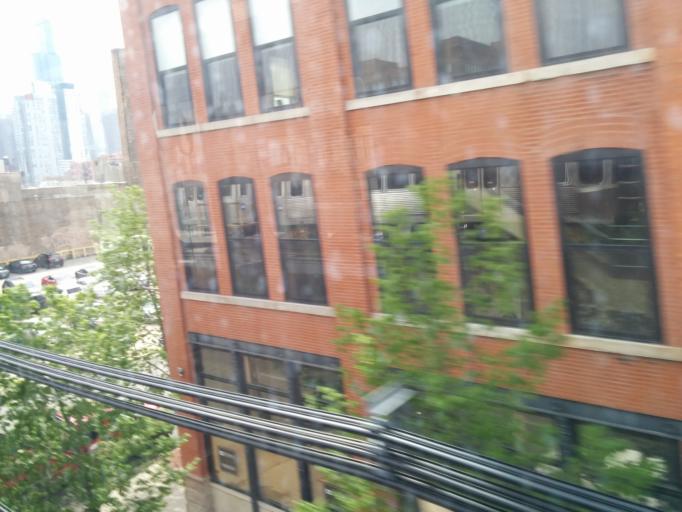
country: US
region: Illinois
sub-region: Cook County
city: Chicago
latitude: 41.8854
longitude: -87.6547
